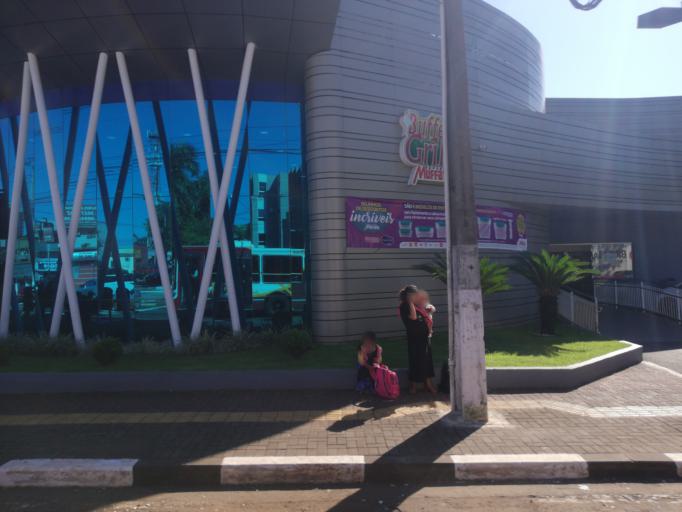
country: BR
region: Parana
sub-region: Foz Do Iguacu
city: Foz do Iguacu
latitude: -25.5469
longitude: -54.5780
